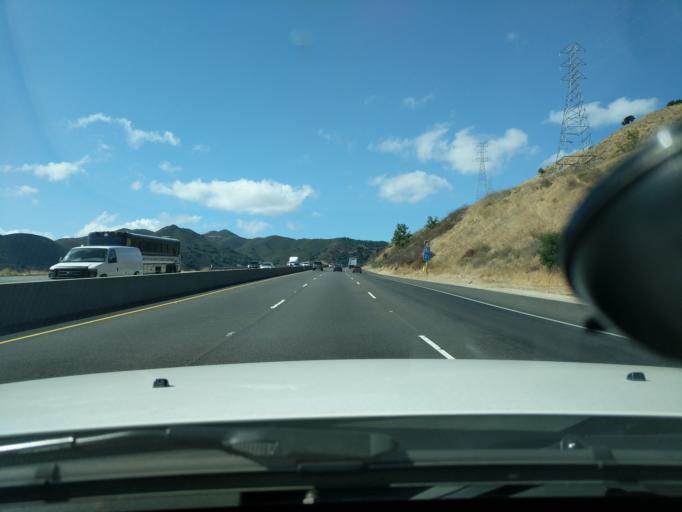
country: US
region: California
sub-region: San Luis Obispo County
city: San Luis Obispo
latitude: 35.3297
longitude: -120.6213
